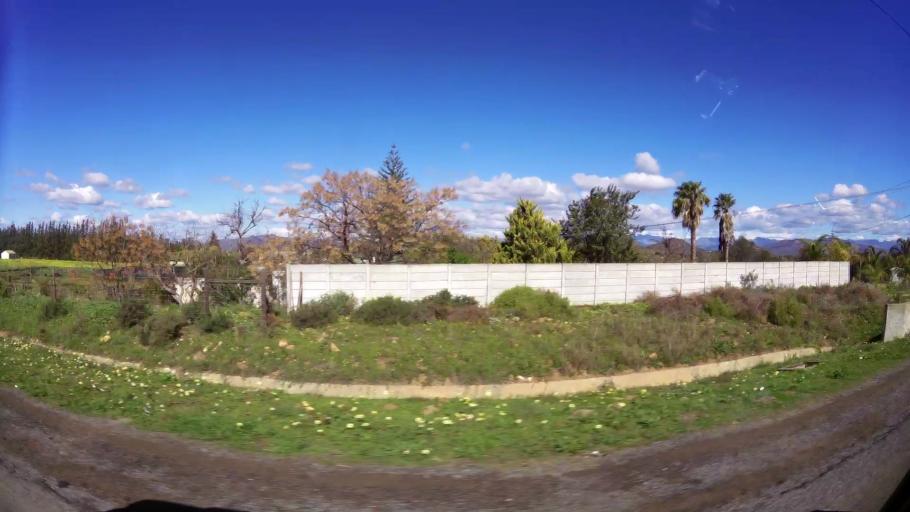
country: ZA
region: Western Cape
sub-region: Cape Winelands District Municipality
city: Ashton
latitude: -33.7957
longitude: 19.8928
